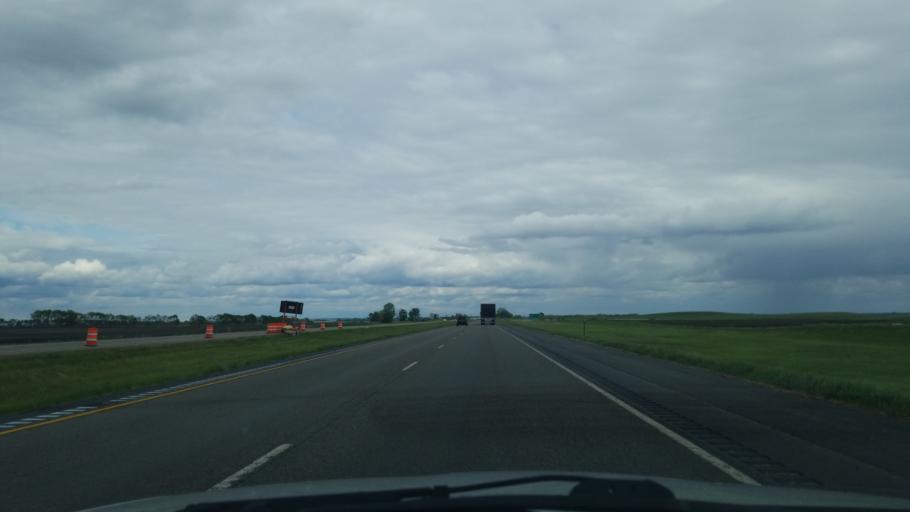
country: US
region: North Dakota
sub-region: Barnes County
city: Valley City
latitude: 46.9198
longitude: -97.7718
